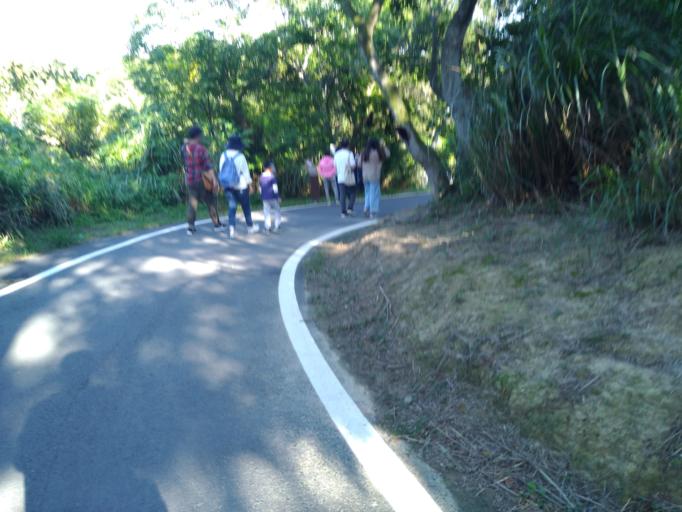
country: TW
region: Taiwan
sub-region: Hsinchu
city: Hsinchu
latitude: 24.7725
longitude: 120.9270
